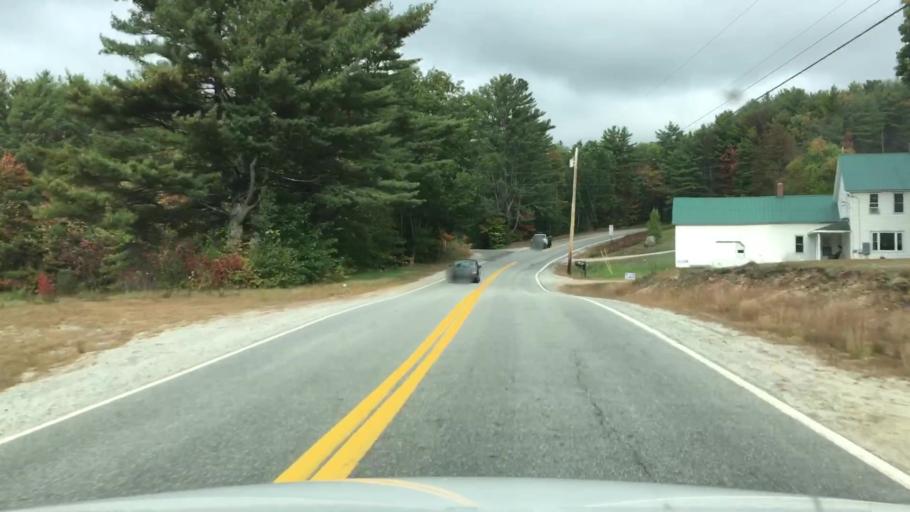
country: US
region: Maine
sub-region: Oxford County
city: Bethel
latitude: 44.3393
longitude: -70.7818
